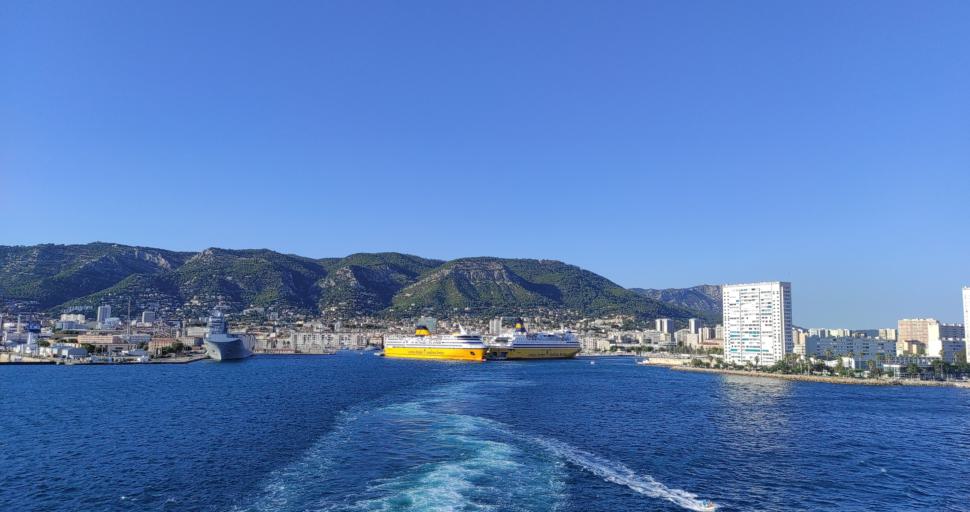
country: FR
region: Provence-Alpes-Cote d'Azur
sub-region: Departement du Var
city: Toulon
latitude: 43.1105
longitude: 5.9251
